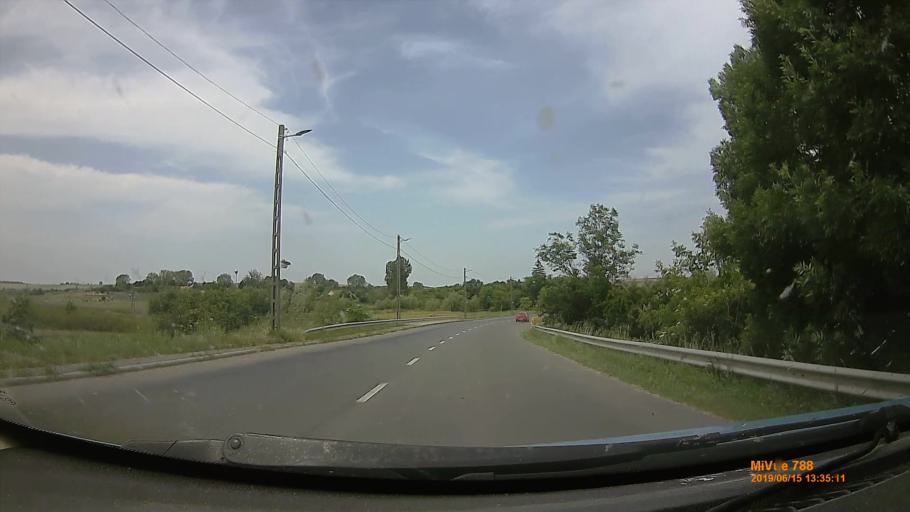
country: HU
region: Tolna
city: Tamasi
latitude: 46.5948
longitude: 18.2002
